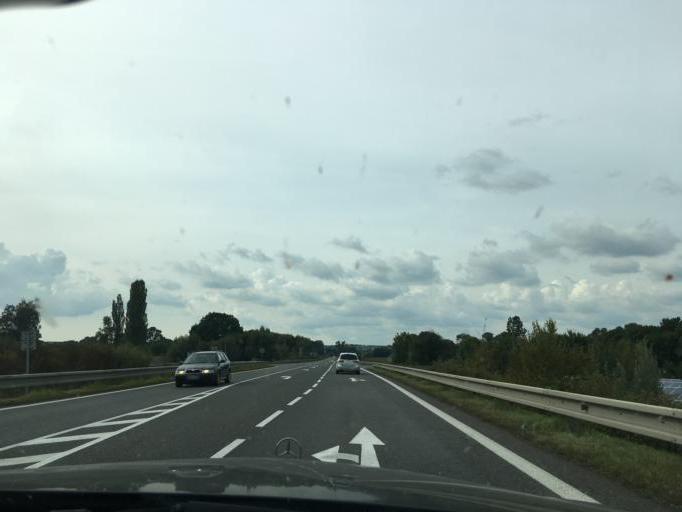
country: CZ
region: Kralovehradecky
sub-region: Okres Nachod
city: Ceska Skalice
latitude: 50.3866
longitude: 16.0289
